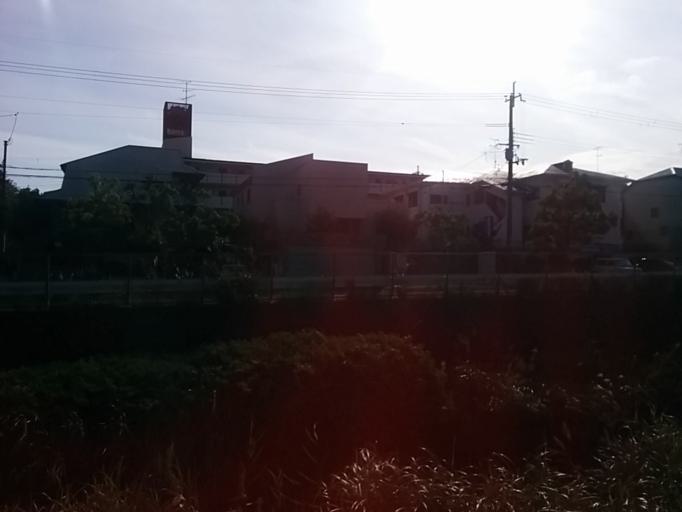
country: JP
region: Nara
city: Nara-shi
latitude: 34.7219
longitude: 135.7920
